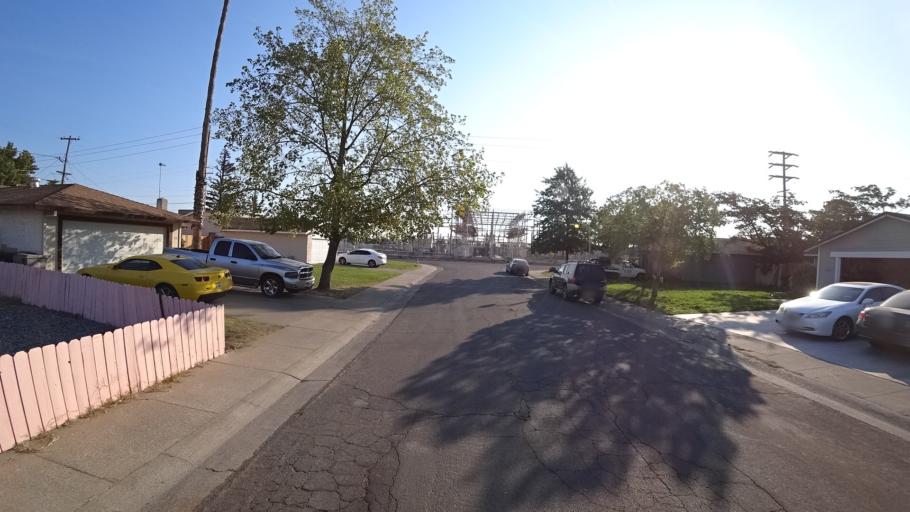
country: US
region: California
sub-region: Sacramento County
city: Parkway
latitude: 38.4898
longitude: -121.4716
